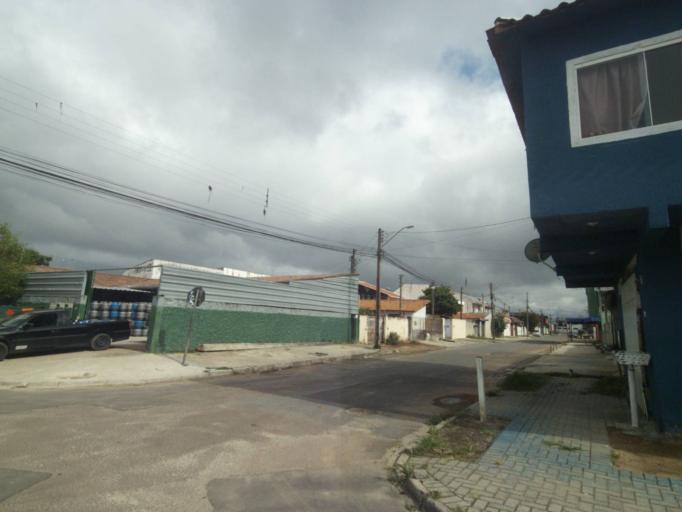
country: BR
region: Parana
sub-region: Pinhais
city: Pinhais
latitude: -25.4570
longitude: -49.2005
